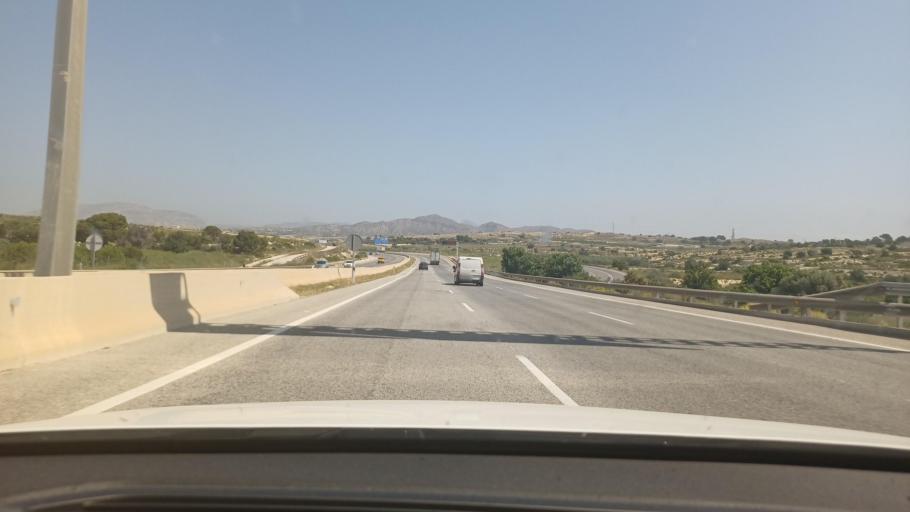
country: ES
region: Valencia
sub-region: Provincia de Alicante
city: Elche
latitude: 38.3265
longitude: -0.6629
